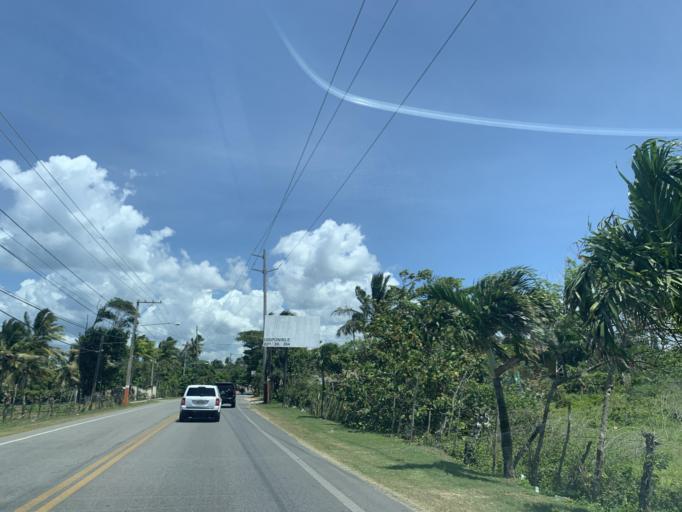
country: DO
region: Puerto Plata
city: Cabarete
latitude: 19.7374
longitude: -70.3904
